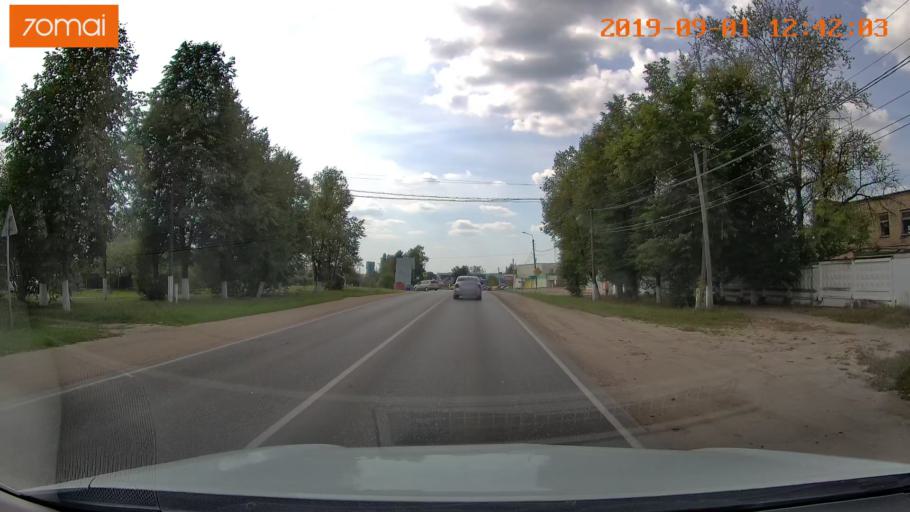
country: RU
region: Kaluga
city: Maloyaroslavets
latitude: 55.0034
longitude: 36.4426
